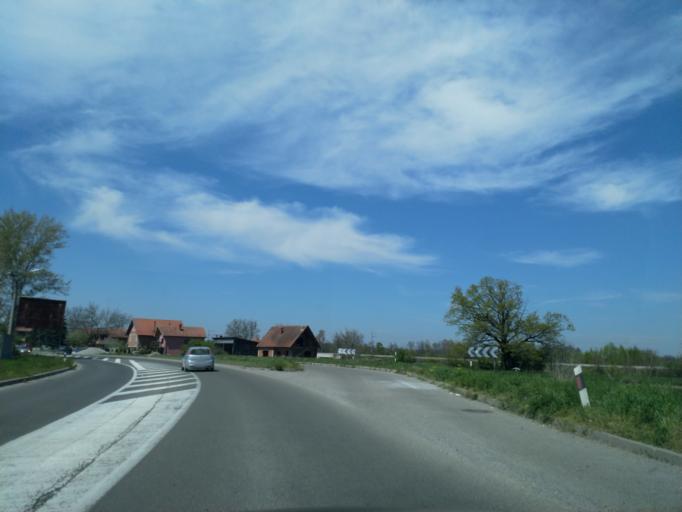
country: RS
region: Central Serbia
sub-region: Kolubarski Okrug
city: Lajkovac
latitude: 44.3701
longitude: 20.1910
